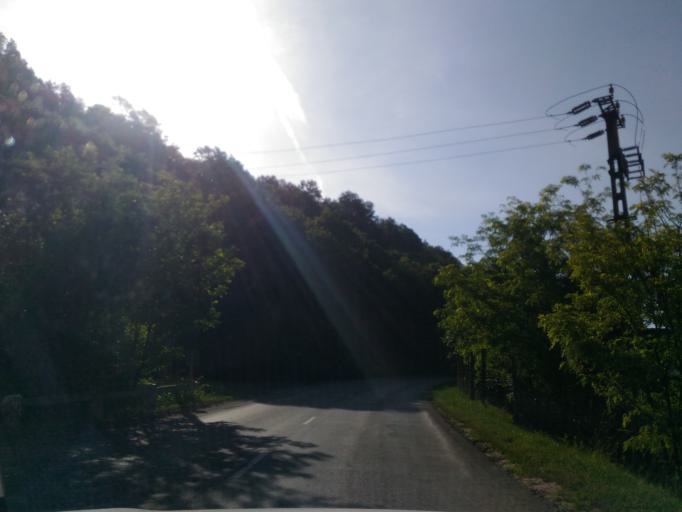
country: HU
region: Baranya
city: Komlo
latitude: 46.1915
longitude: 18.2764
